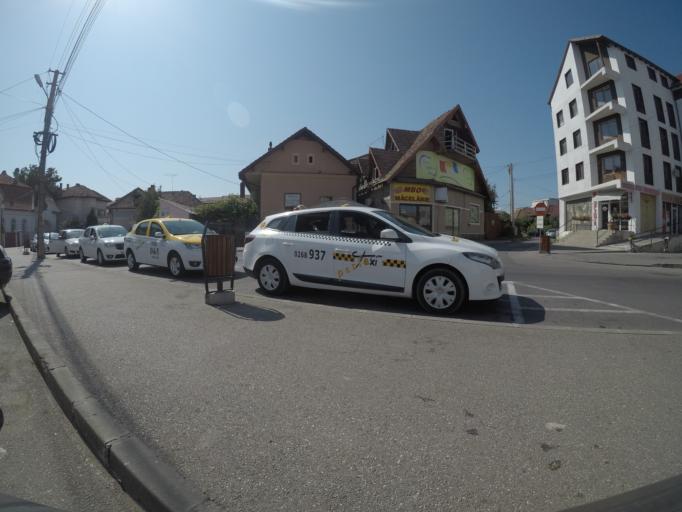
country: RO
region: Brasov
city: Fogarasch
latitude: 45.8422
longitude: 24.9723
